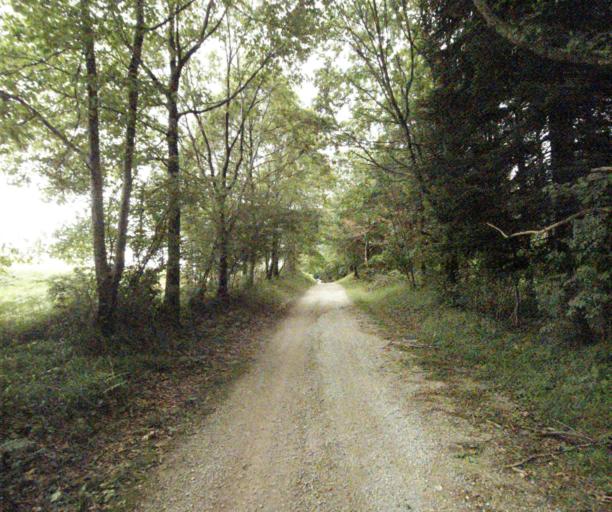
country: FR
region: Midi-Pyrenees
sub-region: Departement du Tarn
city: Soreze
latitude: 43.4278
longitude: 2.1077
